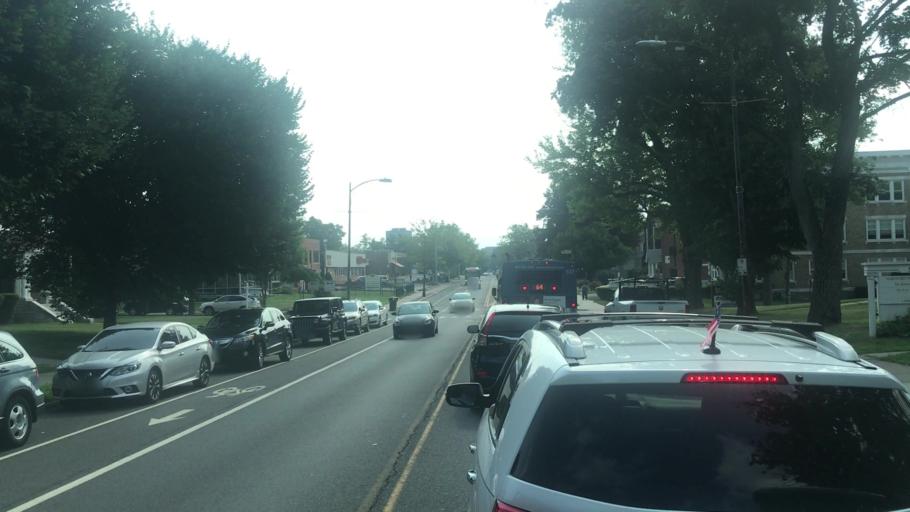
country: US
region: Connecticut
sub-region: Hartford County
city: Hartford
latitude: 41.7660
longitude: -72.7131
